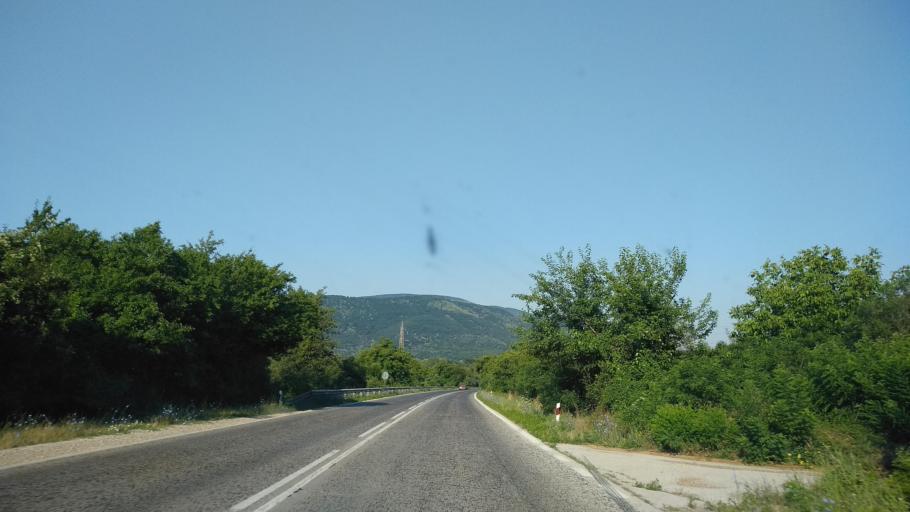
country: BG
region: Lovech
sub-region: Obshtina Lovech
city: Lovech
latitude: 43.0420
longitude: 24.7400
